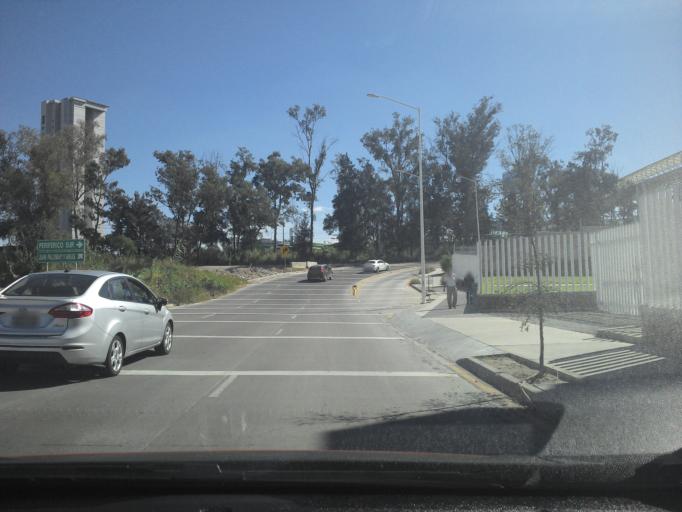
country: MX
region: Jalisco
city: Zapopan2
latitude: 20.7197
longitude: -103.4263
